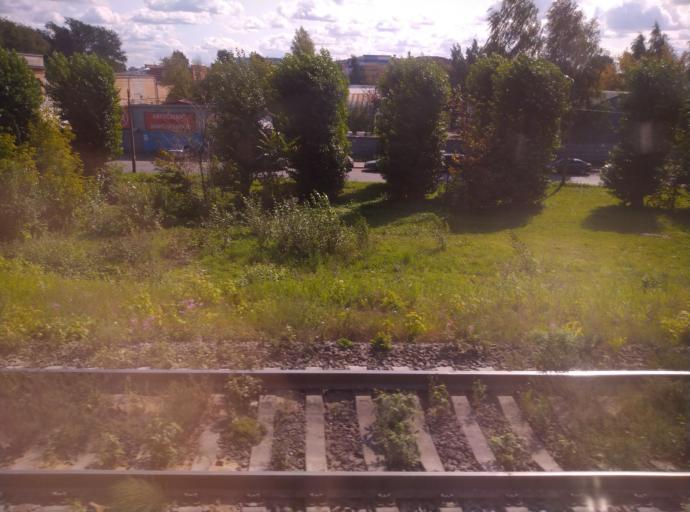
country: RU
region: St.-Petersburg
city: Centralniy
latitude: 59.9067
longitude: 30.3833
